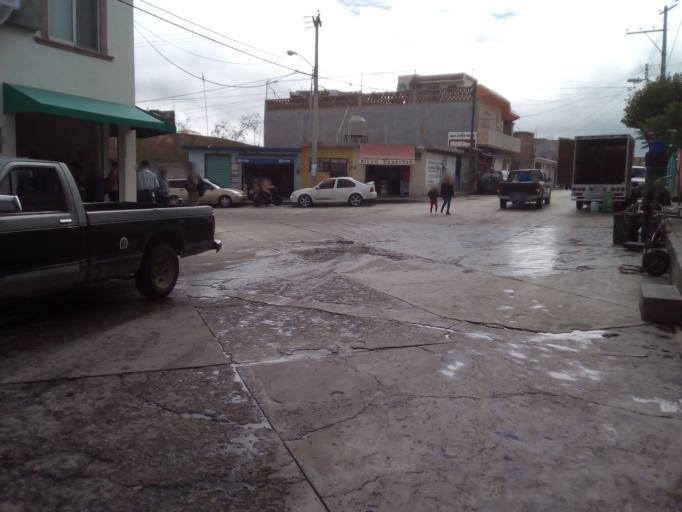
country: MX
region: Guerrero
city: San Luis de la Paz
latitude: 21.2924
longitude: -100.5110
